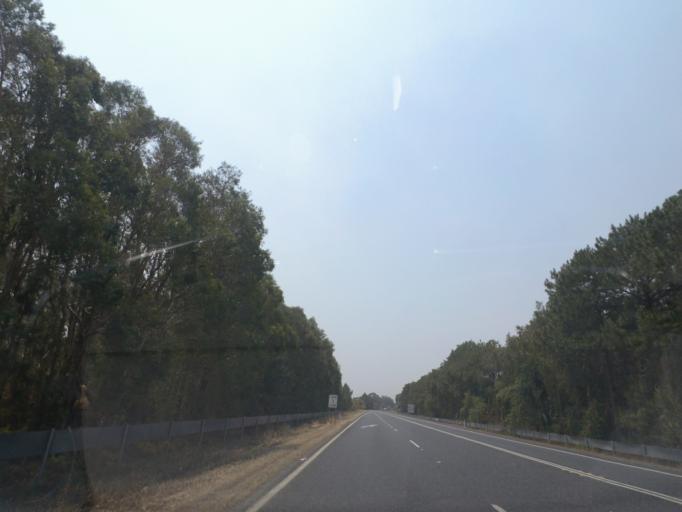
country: AU
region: New South Wales
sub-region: Ballina
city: Ballina
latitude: -28.9387
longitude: 153.4702
